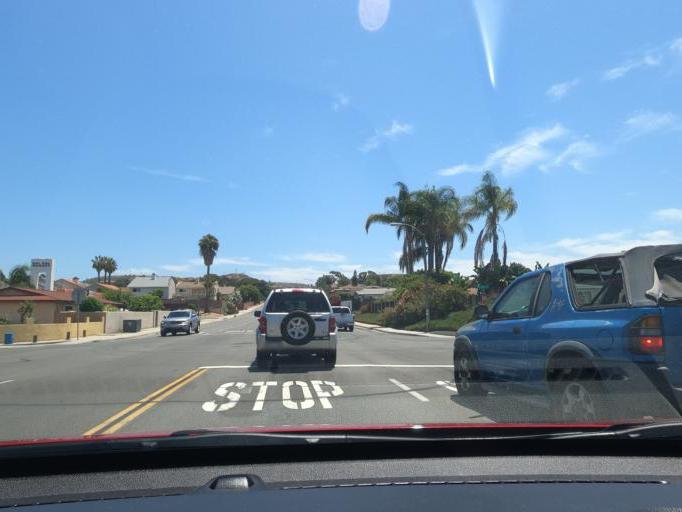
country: US
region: California
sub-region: San Diego County
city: Imperial Beach
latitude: 32.5736
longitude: -117.0437
